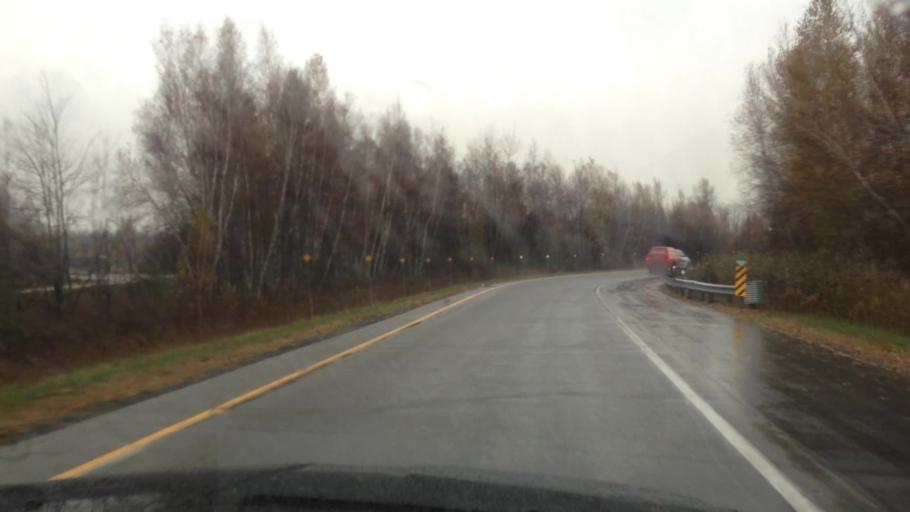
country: CA
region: Ontario
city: Bourget
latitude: 45.3116
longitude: -75.2428
